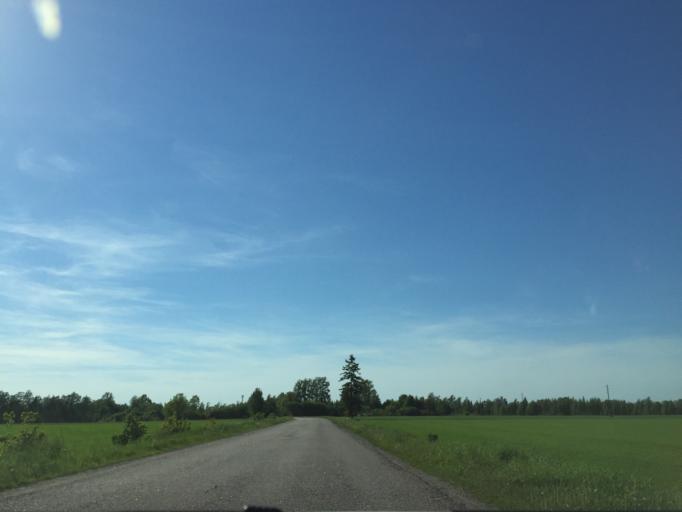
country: LV
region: Jelgava
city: Jelgava
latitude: 56.5274
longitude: 23.7133
